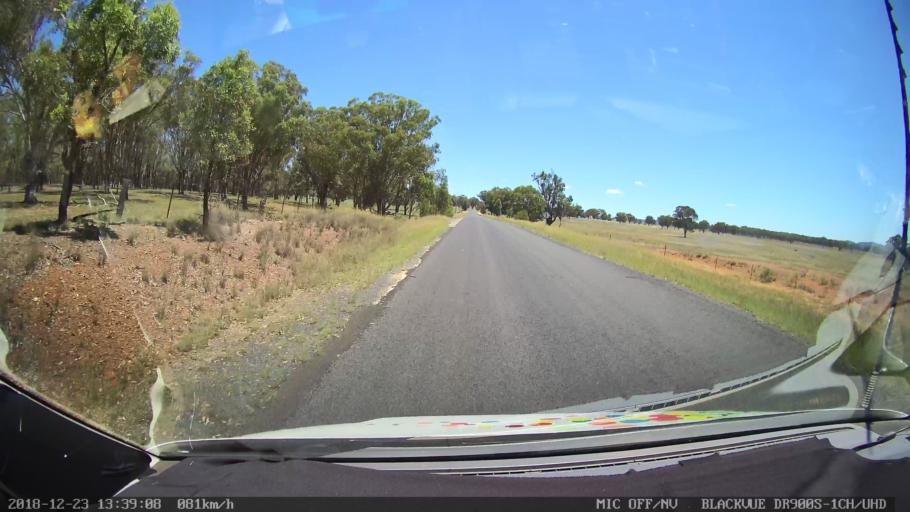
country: AU
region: New South Wales
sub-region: Armidale Dumaresq
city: Armidale
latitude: -30.4555
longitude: 151.2054
